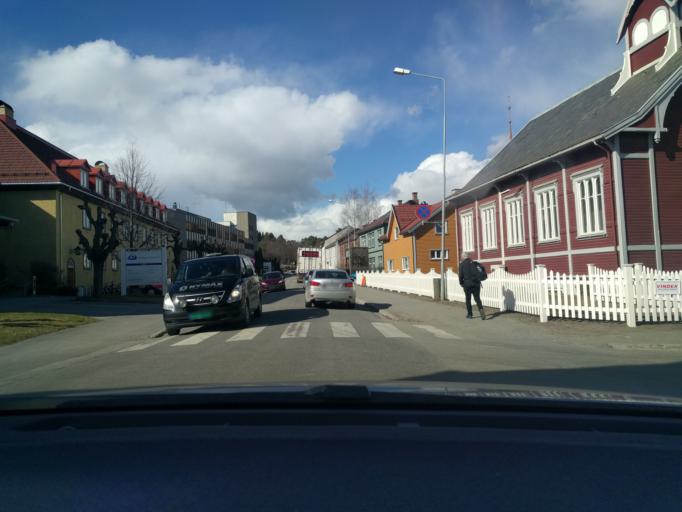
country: NO
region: Hedmark
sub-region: Hamar
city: Hamar
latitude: 60.7971
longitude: 11.0728
